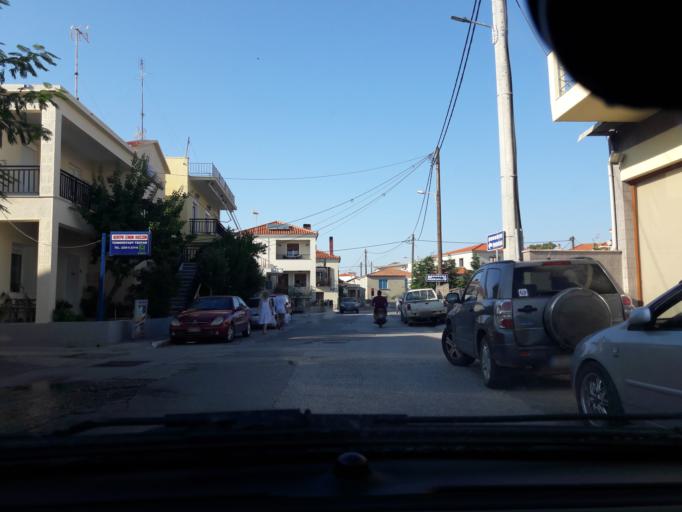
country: GR
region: North Aegean
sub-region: Nomos Lesvou
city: Myrina
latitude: 39.8733
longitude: 25.0623
